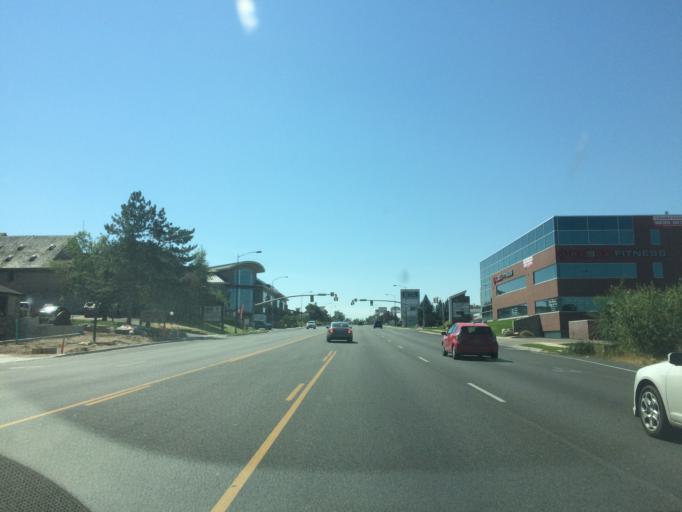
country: US
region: Utah
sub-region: Weber County
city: South Ogden
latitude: 41.1809
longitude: -111.9492
